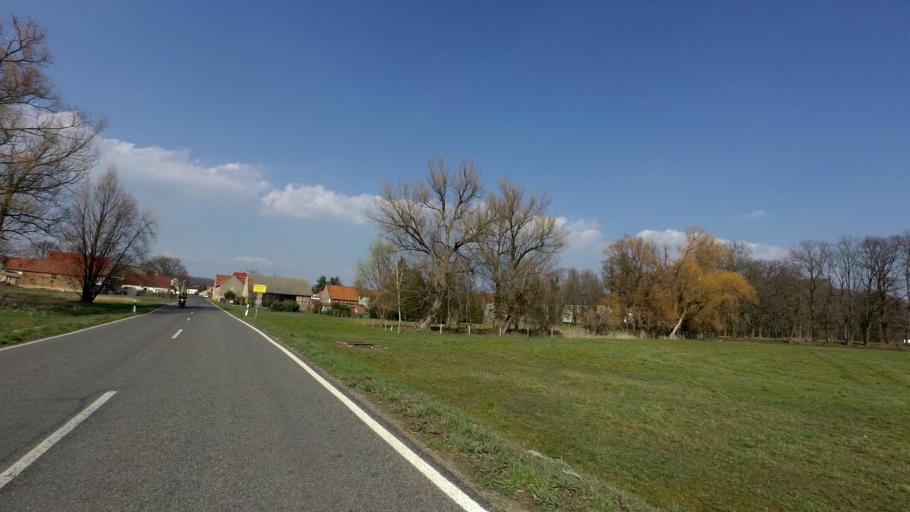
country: DE
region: Brandenburg
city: Dahme
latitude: 51.9023
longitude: 13.4873
